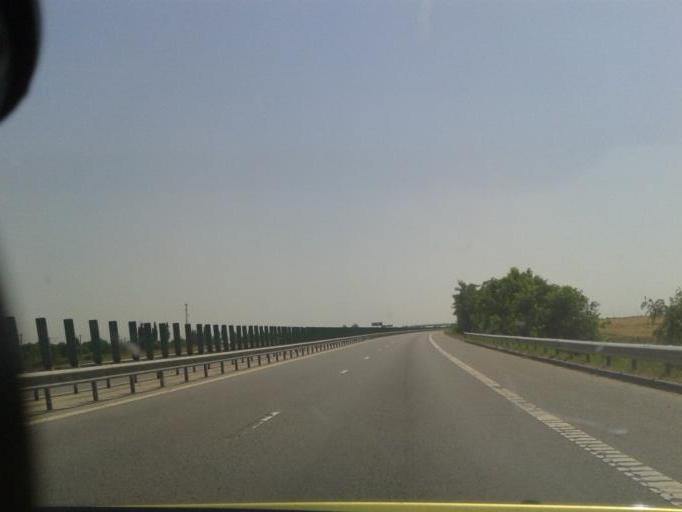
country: RO
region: Calarasi
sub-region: Comuna Nicolae Balcescu
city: Nicolae Balcescu
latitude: 44.4454
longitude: 26.7358
